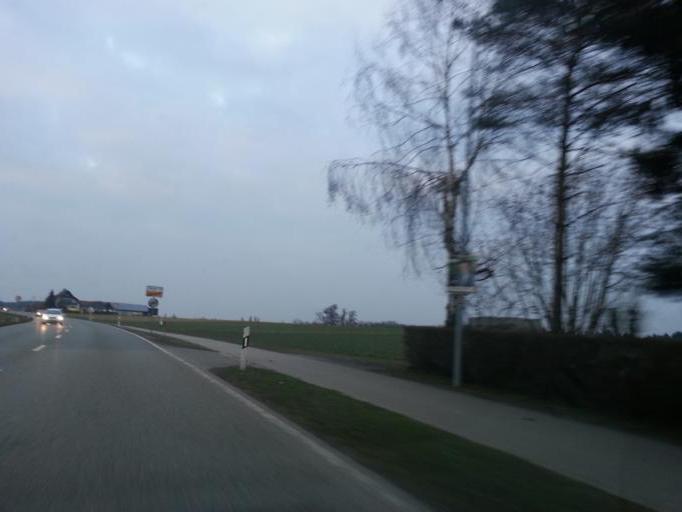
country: DE
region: Baden-Wuerttemberg
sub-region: Tuebingen Region
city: Horgenzell
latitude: 47.7489
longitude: 9.5103
